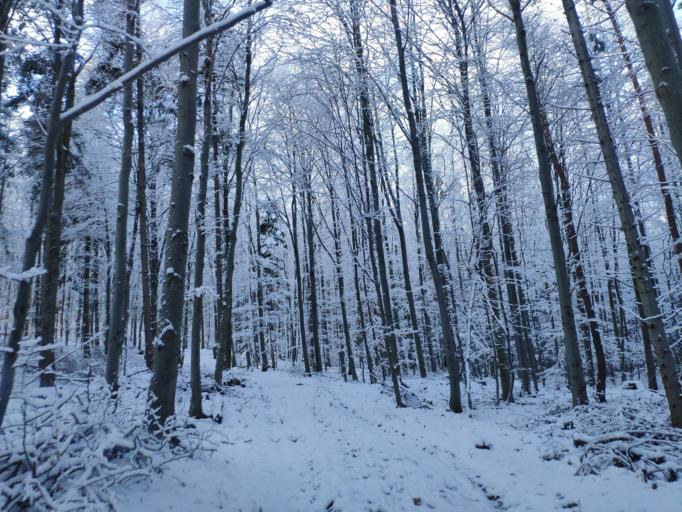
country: SK
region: Kosicky
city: Moldava nad Bodvou
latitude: 48.7462
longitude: 21.0854
